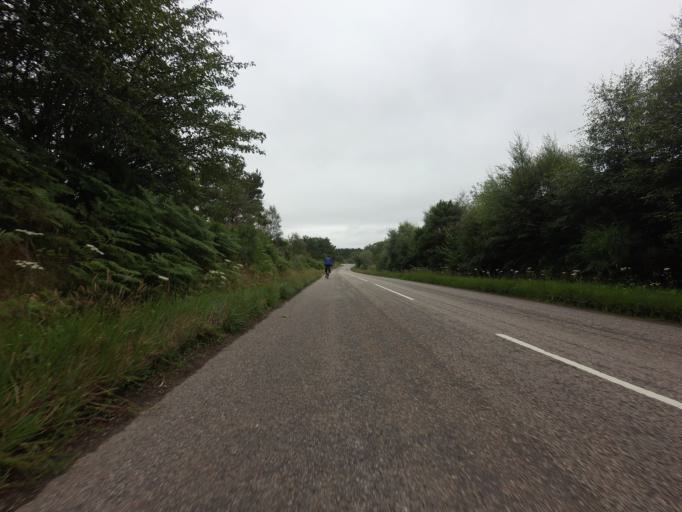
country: GB
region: Scotland
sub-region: Highland
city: Alness
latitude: 58.0154
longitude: -4.4053
